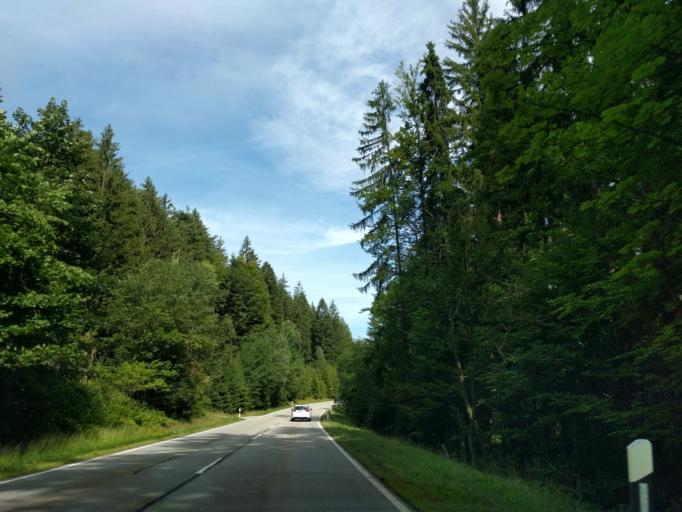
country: DE
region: Bavaria
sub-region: Lower Bavaria
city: Langdorf
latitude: 49.0366
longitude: 13.1194
